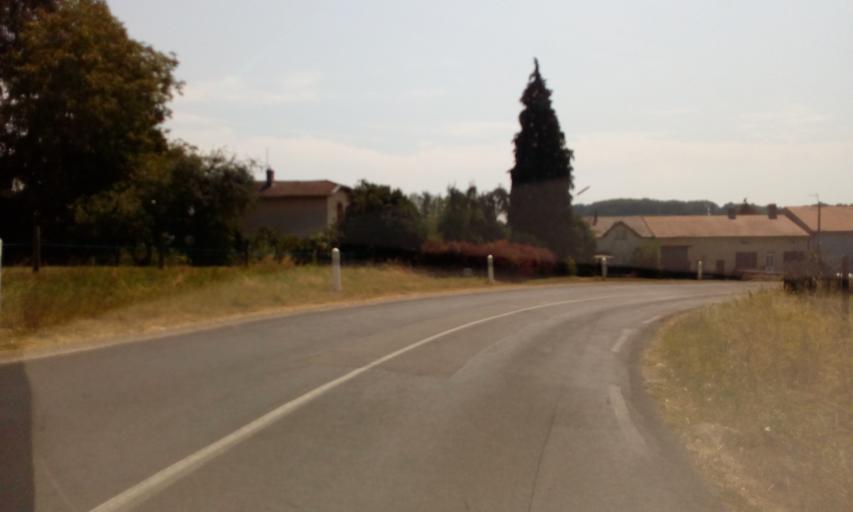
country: FR
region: Lorraine
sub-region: Departement de la Meuse
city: Belleville-sur-Meuse
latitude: 49.2940
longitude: 5.4680
